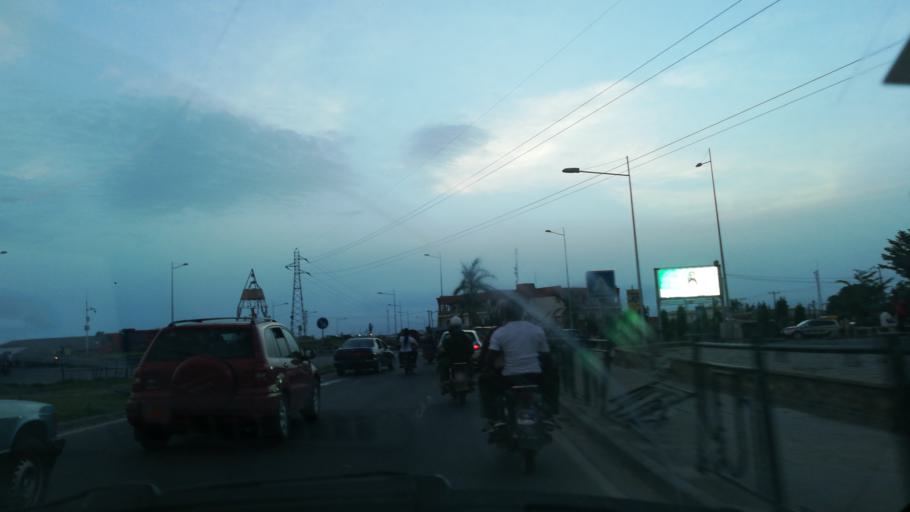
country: CM
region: Littoral
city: Bonaberi
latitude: 4.0699
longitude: 9.6858
